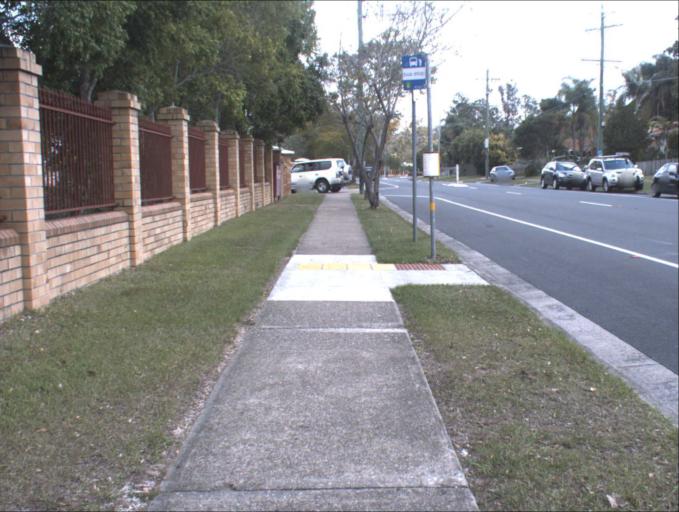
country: AU
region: Queensland
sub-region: Logan
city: Park Ridge South
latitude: -27.6874
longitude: 153.0300
